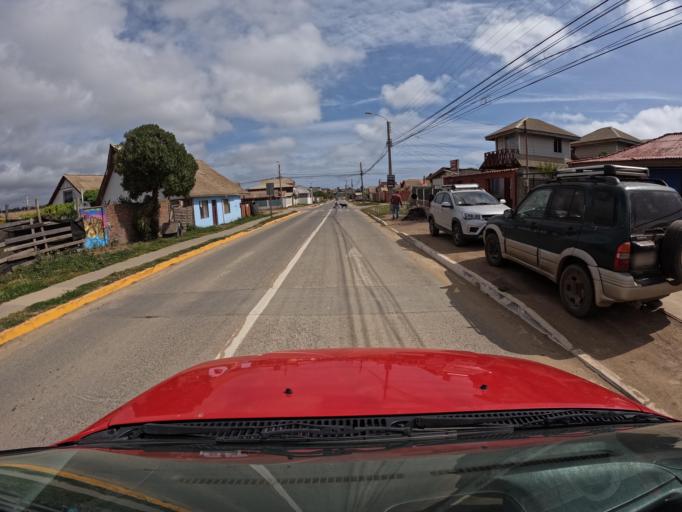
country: CL
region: O'Higgins
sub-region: Provincia de Colchagua
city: Santa Cruz
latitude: -34.3834
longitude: -72.0157
